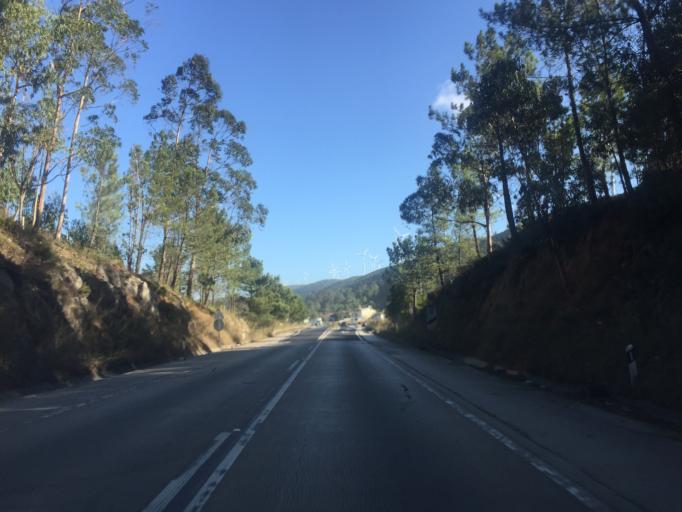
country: PT
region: Santarem
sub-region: Rio Maior
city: Rio Maior
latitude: 39.3724
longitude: -8.9655
